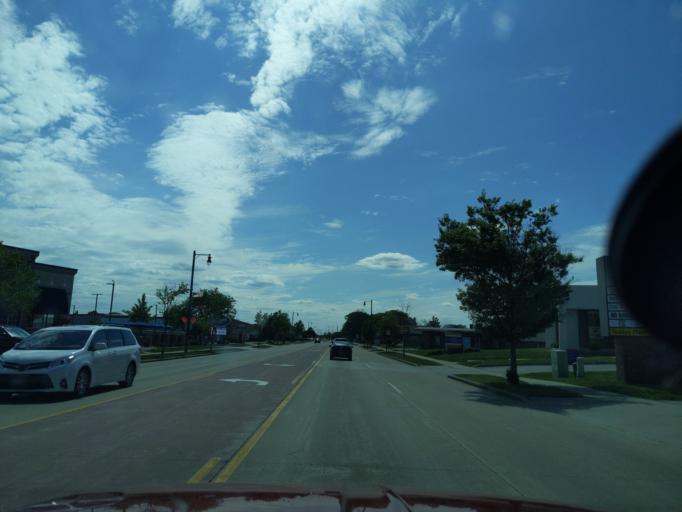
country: US
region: Wisconsin
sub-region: Dane County
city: Sun Prairie
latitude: 43.1787
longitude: -89.2383
